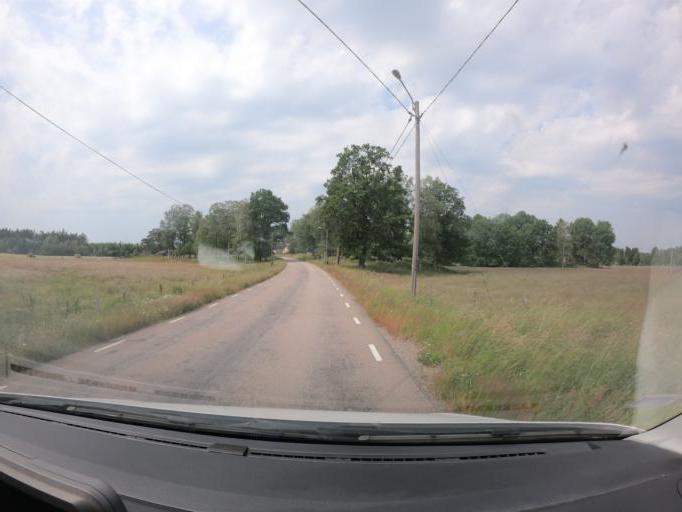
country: SE
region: Skane
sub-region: Hassleholms Kommun
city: Bjarnum
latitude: 56.3303
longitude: 13.5991
